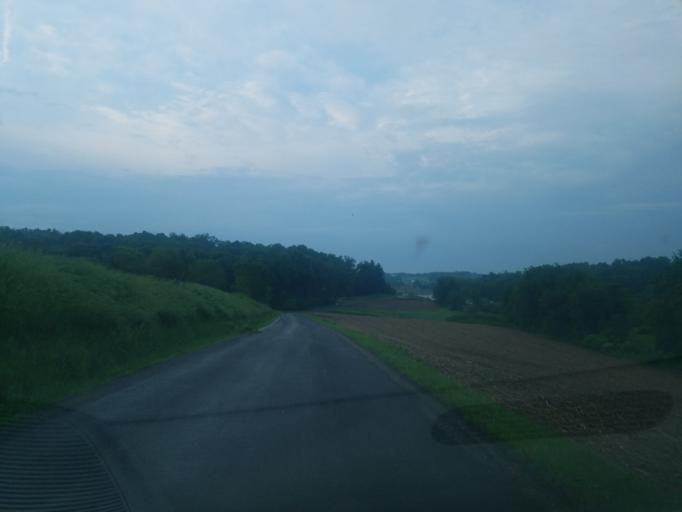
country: US
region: Ohio
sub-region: Stark County
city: Minerva
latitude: 40.7592
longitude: -80.9503
